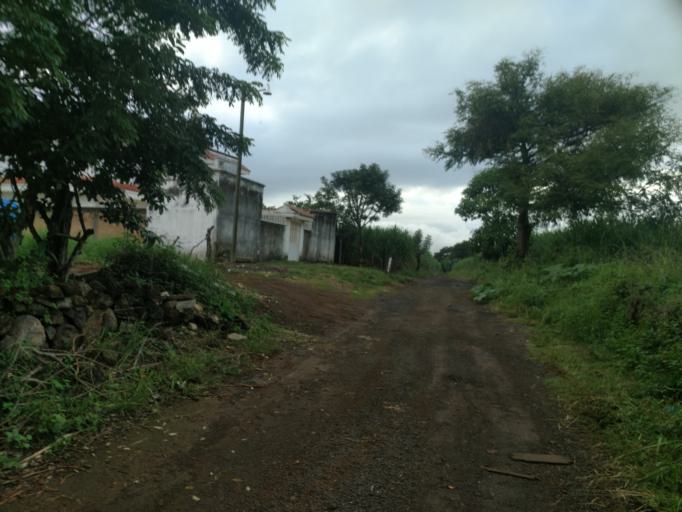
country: MX
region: Nayarit
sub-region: Tepic
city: La Corregidora
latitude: 21.4689
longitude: -104.8007
